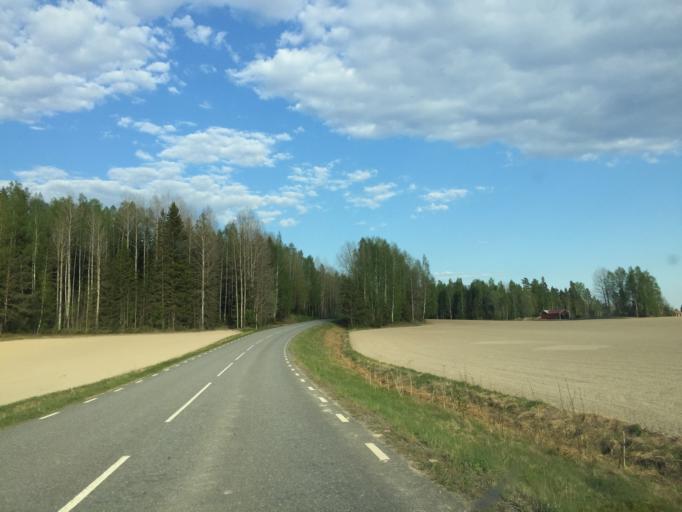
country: SE
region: OErebro
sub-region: Orebro Kommun
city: Hovsta
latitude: 59.3865
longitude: 15.1836
